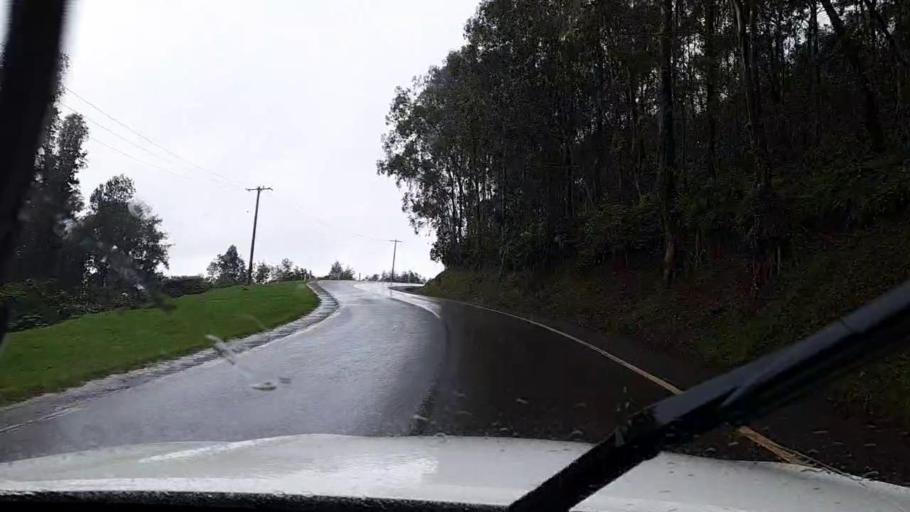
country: RW
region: Western Province
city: Cyangugu
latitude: -2.4624
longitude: 28.9939
